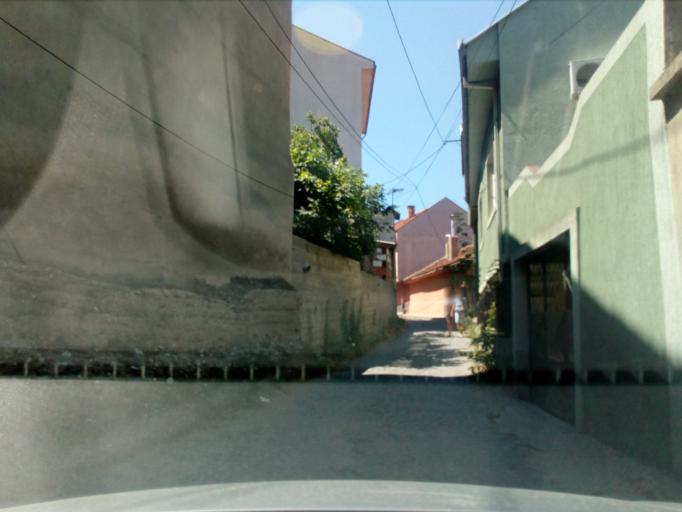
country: MK
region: Veles
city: Veles
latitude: 41.7199
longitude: 21.7897
